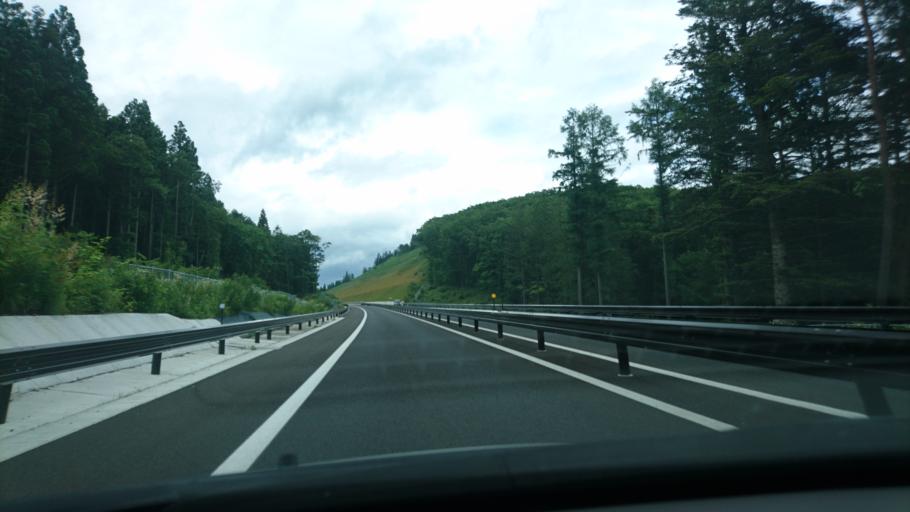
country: JP
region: Iwate
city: Yamada
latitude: 39.5471
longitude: 141.9249
